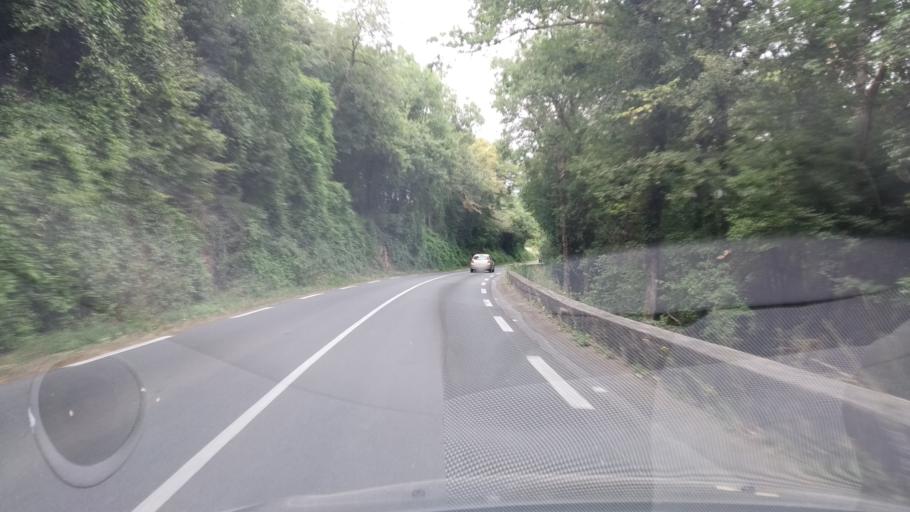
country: FR
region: Poitou-Charentes
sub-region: Departement de la Vienne
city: Saint-Benoit
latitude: 46.5507
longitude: 0.3511
